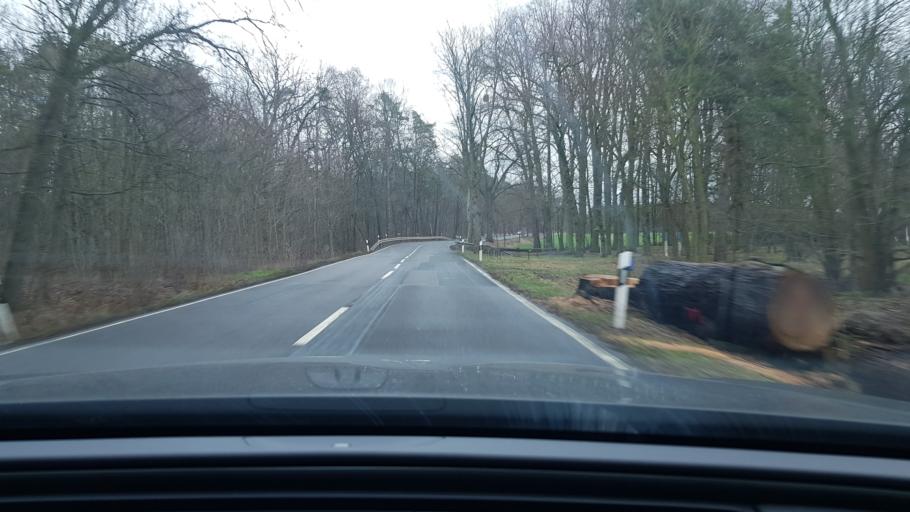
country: DE
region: Lower Saxony
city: Bahrdorf
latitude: 52.4203
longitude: 11.0344
